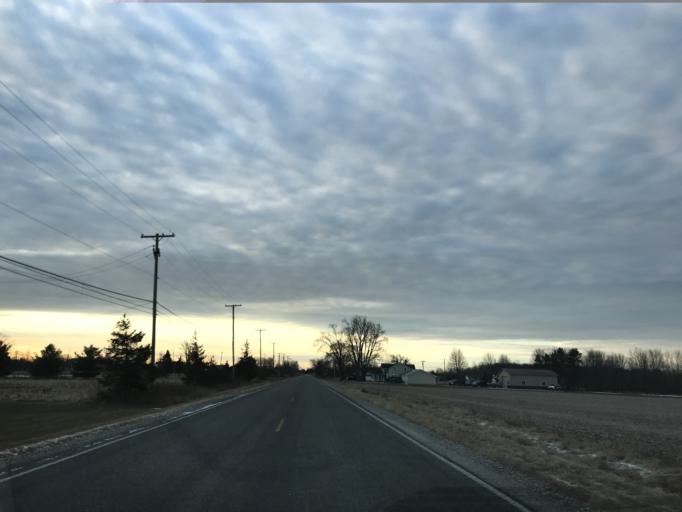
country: US
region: Michigan
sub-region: Macomb County
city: Armada
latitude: 42.9005
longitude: -82.8832
